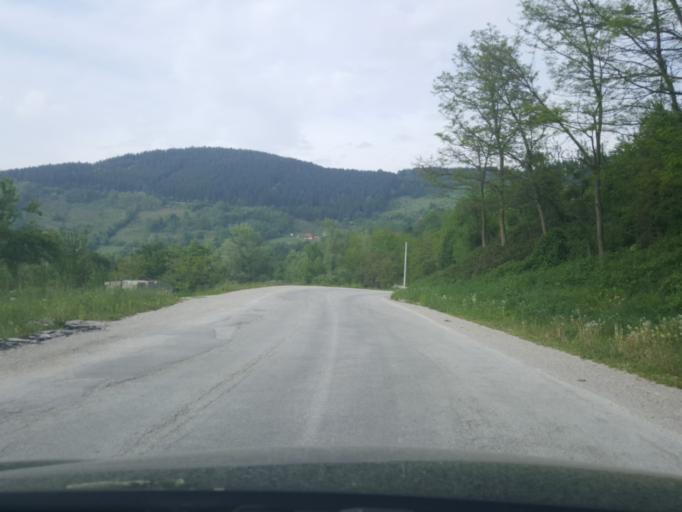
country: RS
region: Central Serbia
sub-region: Zlatiborski Okrug
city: Bajina Basta
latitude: 44.0726
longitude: 19.6608
